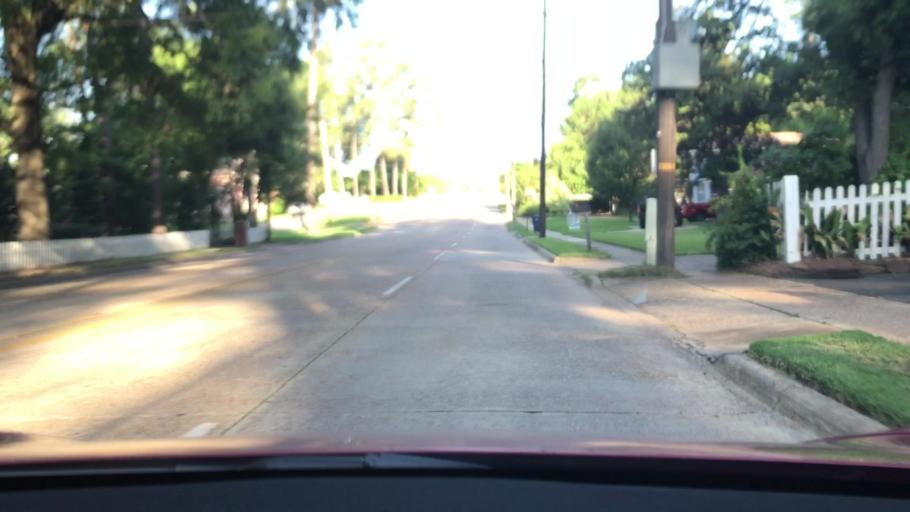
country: US
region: Louisiana
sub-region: Bossier Parish
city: Bossier City
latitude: 32.4548
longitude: -93.7429
